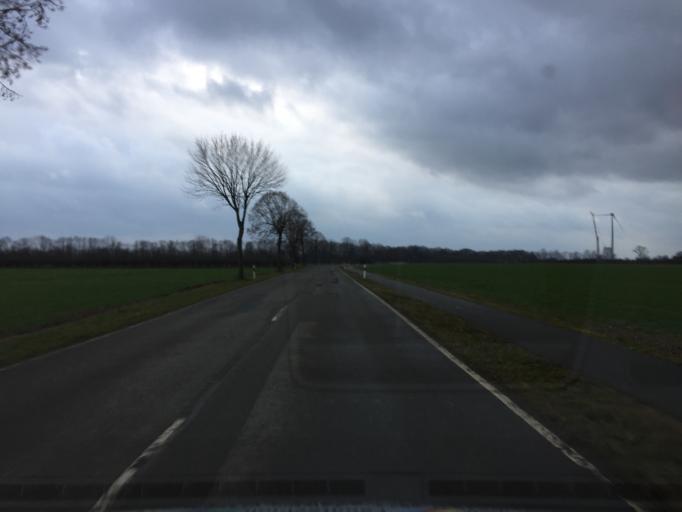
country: DE
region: Lower Saxony
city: Stolzenau
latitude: 52.5034
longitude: 9.0722
